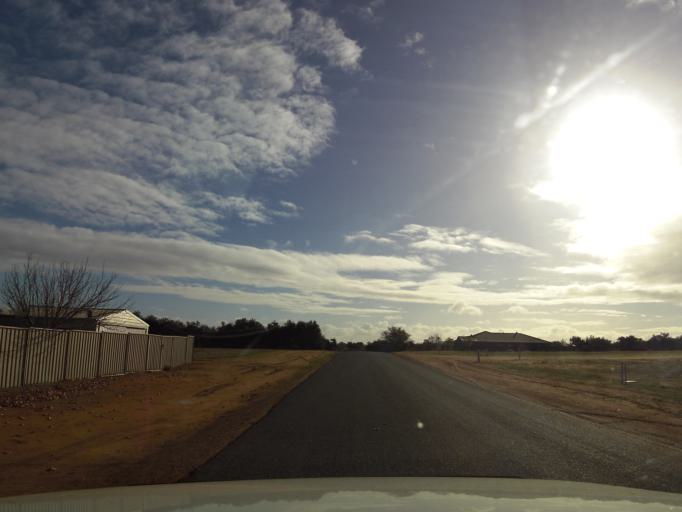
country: AU
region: South Australia
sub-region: Berri and Barmera
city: Berri
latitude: -34.2814
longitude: 140.5820
